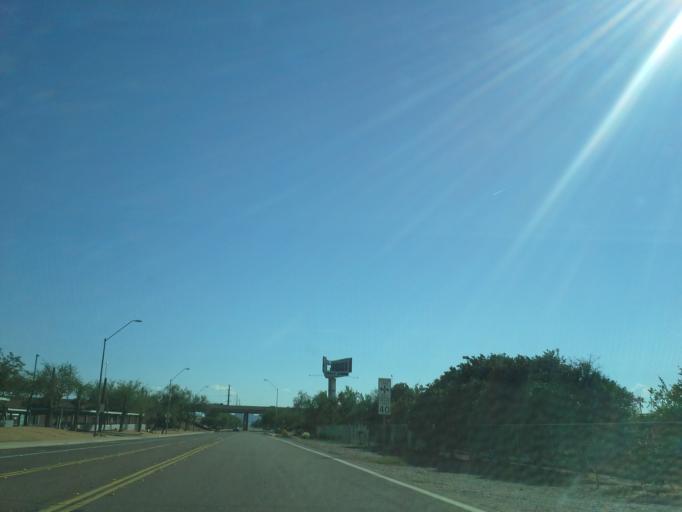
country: US
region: Arizona
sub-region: Maricopa County
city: Paradise Valley
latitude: 33.6753
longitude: -112.0138
